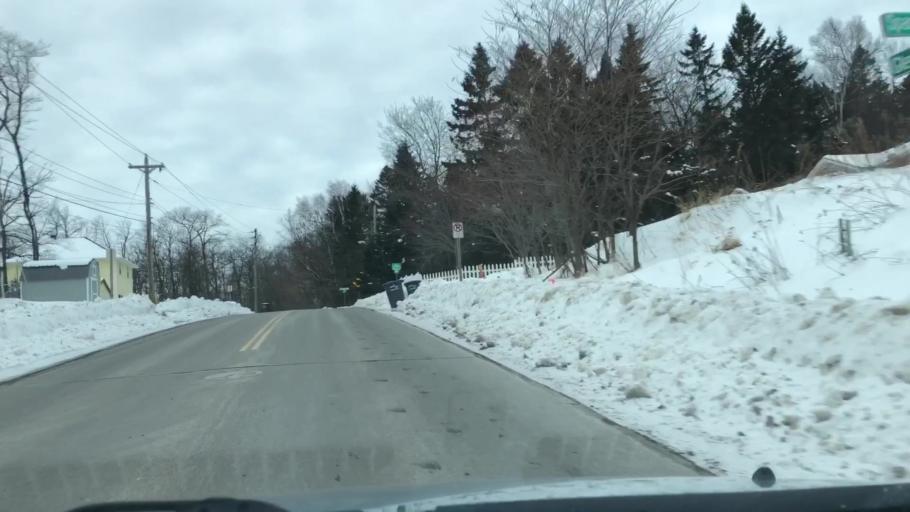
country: US
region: Minnesota
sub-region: Saint Louis County
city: Arnold
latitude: 46.8367
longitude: -92.0626
